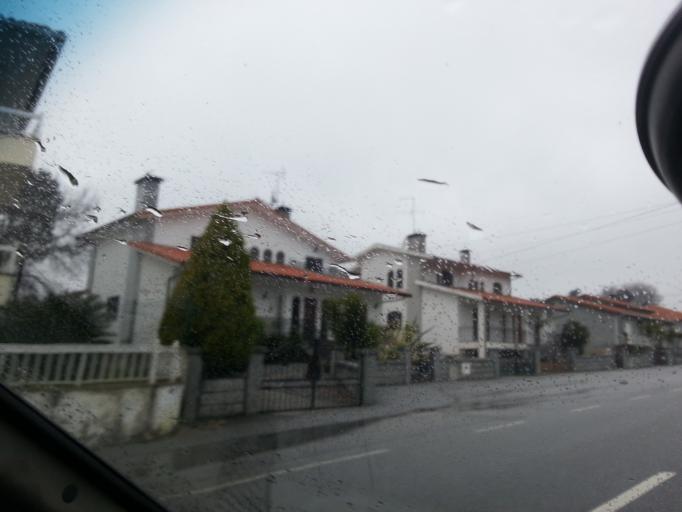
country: PT
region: Viseu
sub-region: Viseu
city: Rio de Loba
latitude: 40.6558
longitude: -7.8727
